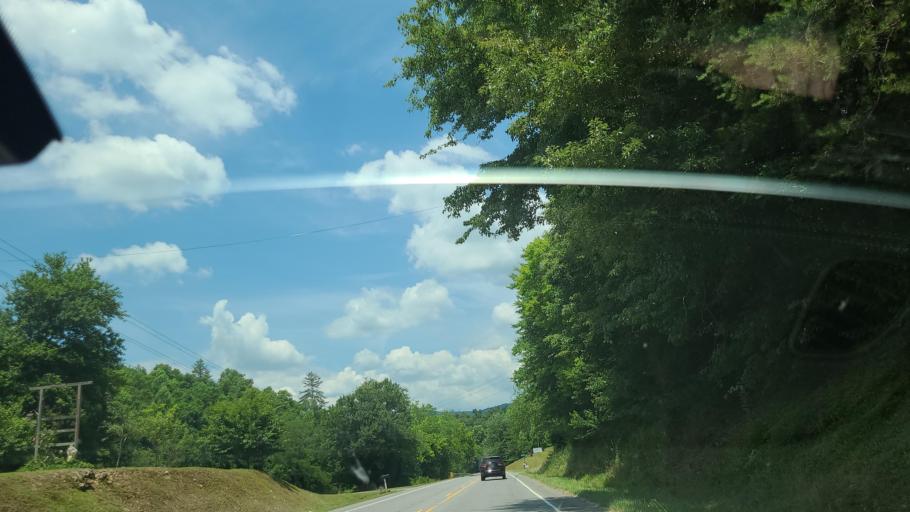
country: US
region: North Carolina
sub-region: Clay County
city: Hayesville
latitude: 35.0486
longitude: -83.8825
